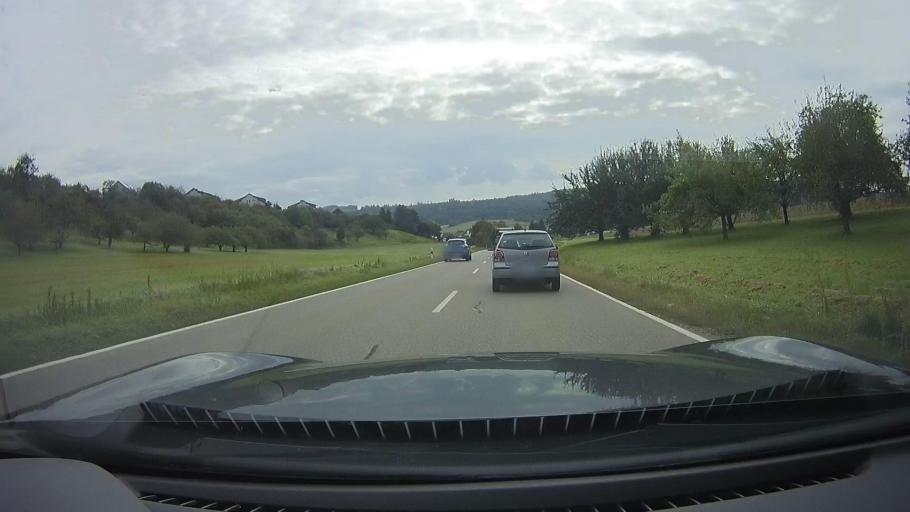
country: DE
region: Baden-Wuerttemberg
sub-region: Regierungsbezirk Stuttgart
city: Abstatt
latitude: 49.0856
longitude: 9.3117
